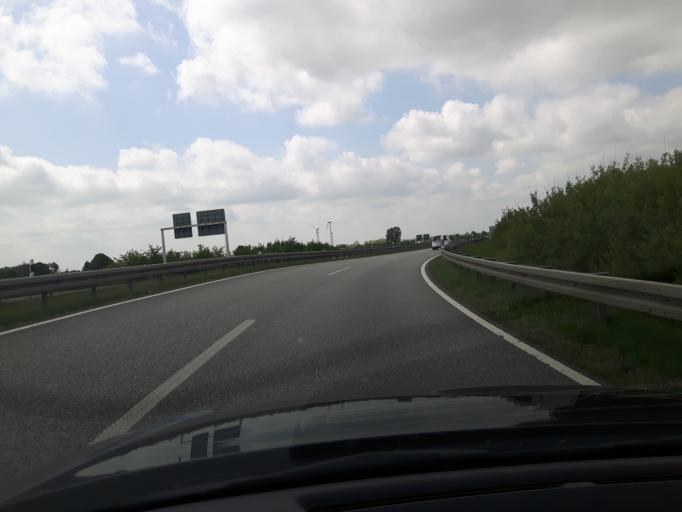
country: DE
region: Mecklenburg-Vorpommern
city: Kavelstorf
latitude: 54.0282
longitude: 12.1967
